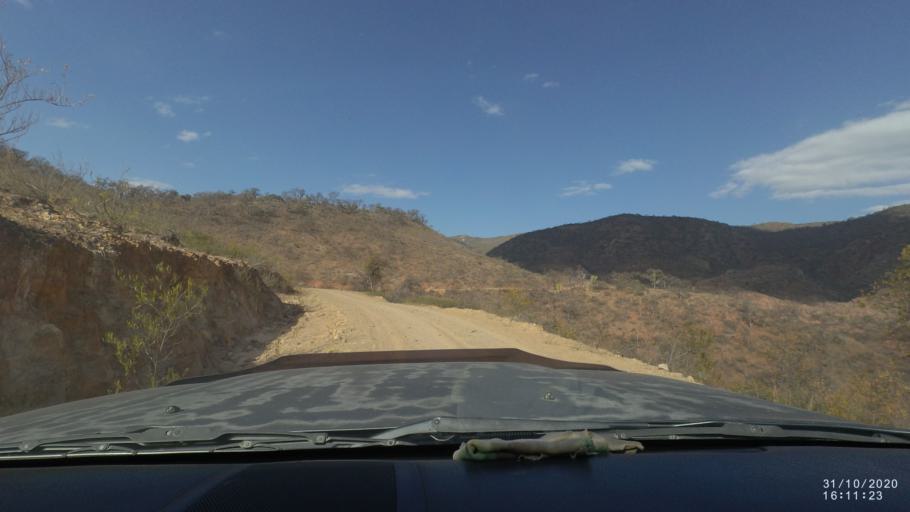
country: BO
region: Chuquisaca
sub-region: Provincia Zudanez
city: Mojocoya
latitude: -18.3803
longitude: -64.6243
